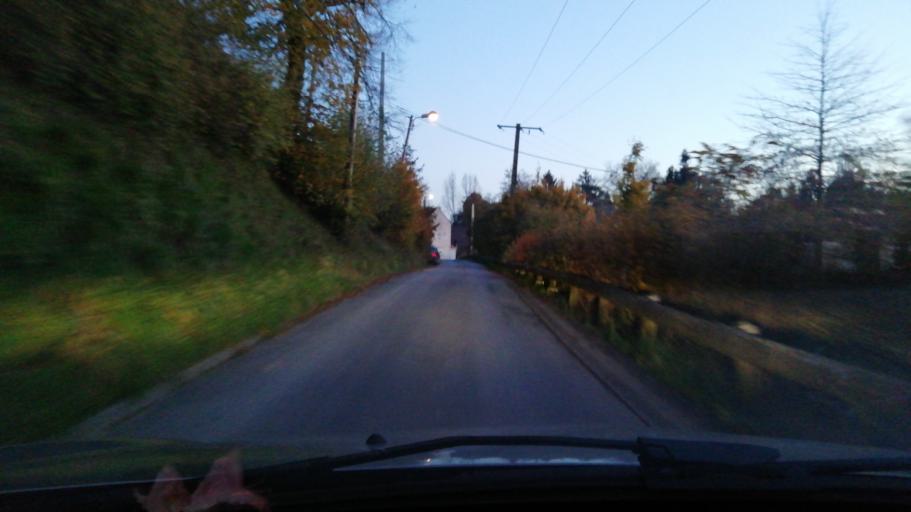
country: FR
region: Nord-Pas-de-Calais
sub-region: Departement du Nord
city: Marpent
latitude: 50.2579
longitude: 4.0784
